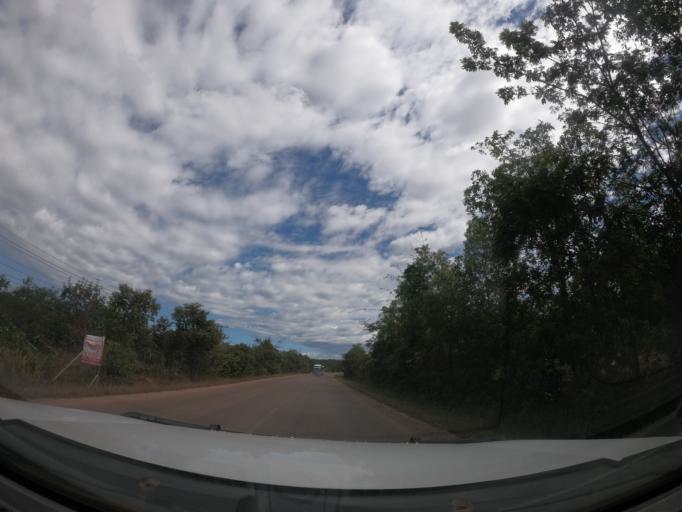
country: LA
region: Bolikhamxai
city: Muang Pakxan
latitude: 18.4439
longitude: 103.5035
